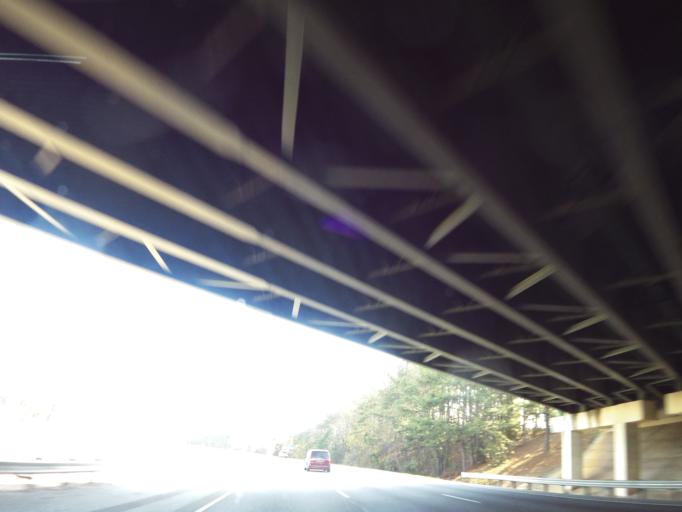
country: US
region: Alabama
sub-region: Russell County
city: Phenix City
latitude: 32.5283
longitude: -84.9597
